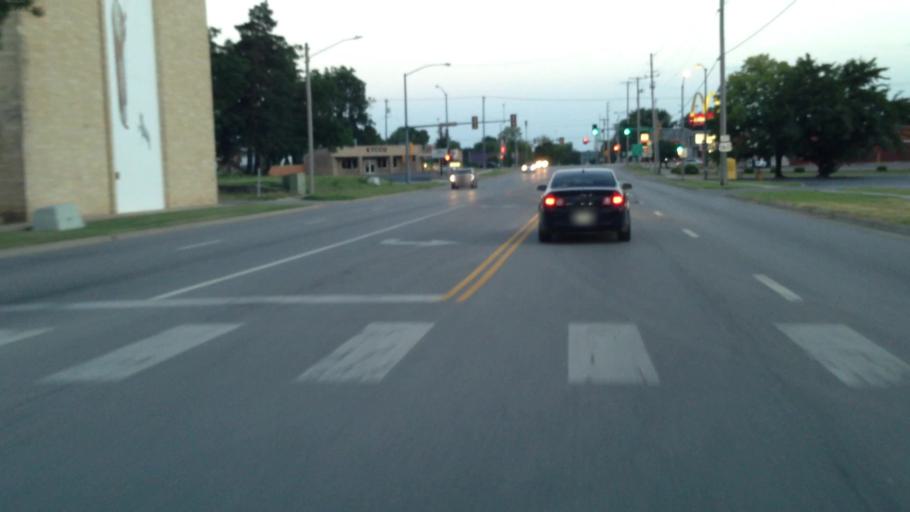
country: US
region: Kansas
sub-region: Montgomery County
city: Independence
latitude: 37.2254
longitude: -95.7108
